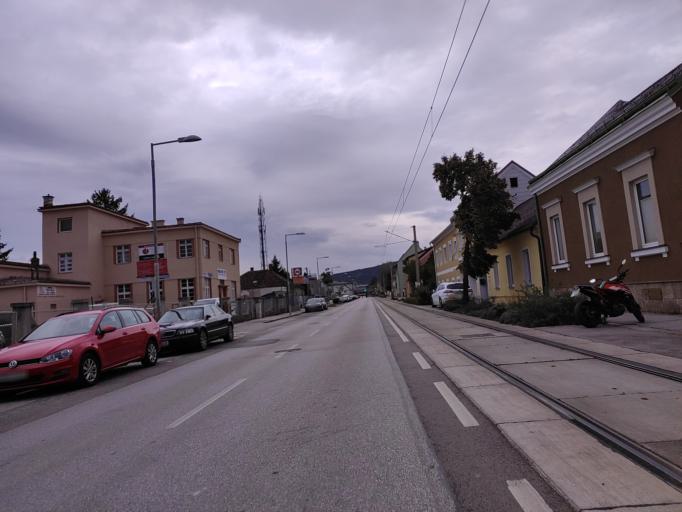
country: AT
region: Lower Austria
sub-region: Politischer Bezirk Baden
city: Baden
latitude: 48.0015
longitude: 16.2471
